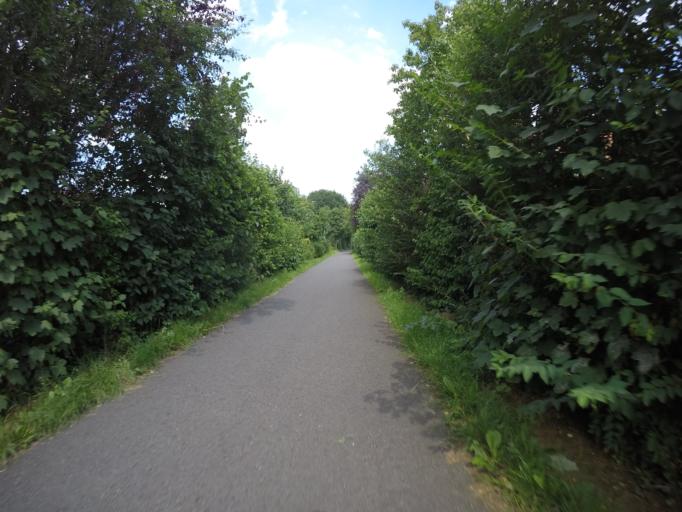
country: DE
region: North Rhine-Westphalia
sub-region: Regierungsbezirk Munster
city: Borken
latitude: 51.8472
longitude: 6.8424
